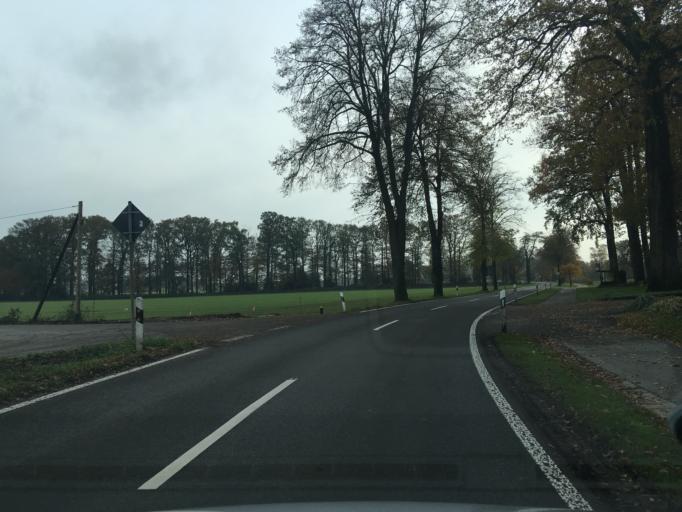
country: DE
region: North Rhine-Westphalia
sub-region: Regierungsbezirk Munster
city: Velen
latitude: 51.9285
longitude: 6.9509
